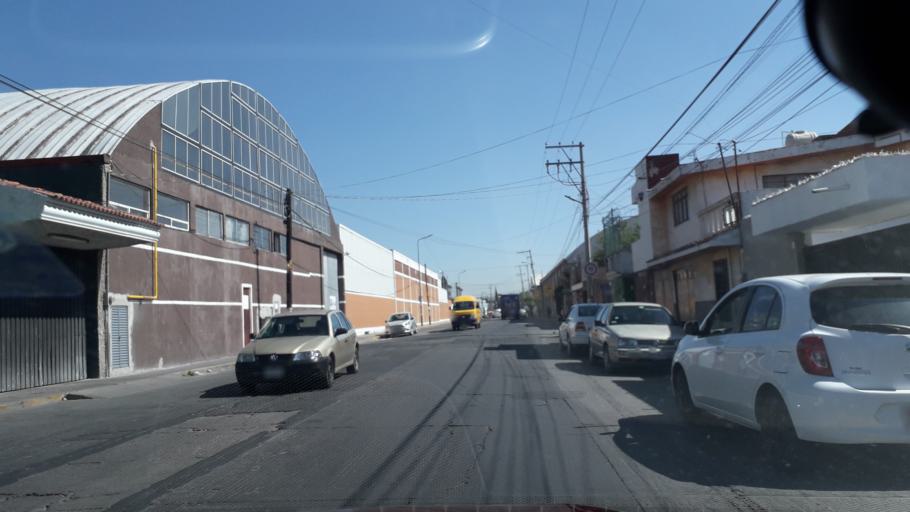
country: MX
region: Puebla
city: Puebla
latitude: 19.0793
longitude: -98.2116
